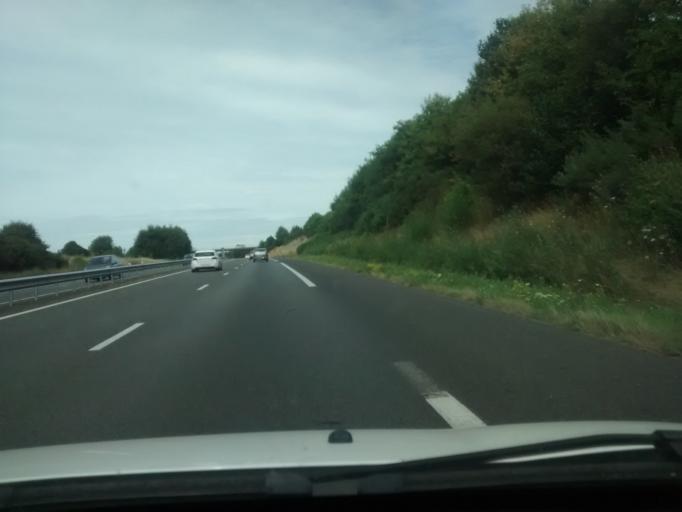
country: FR
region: Lower Normandy
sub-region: Departement de la Manche
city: Saint-James
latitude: 48.4804
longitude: -1.3290
